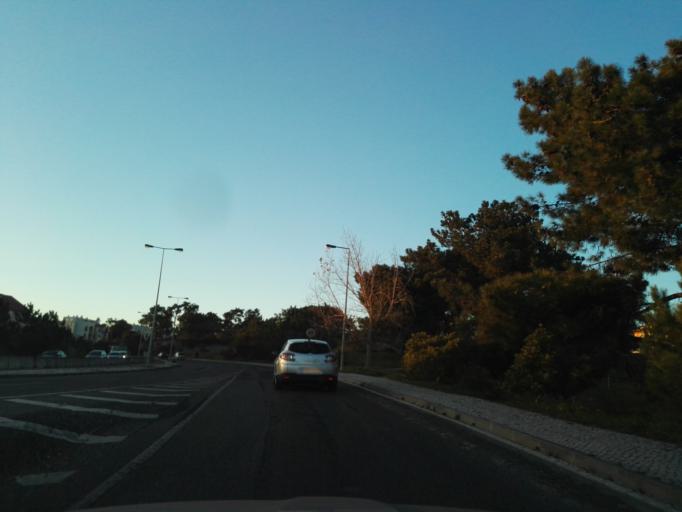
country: PT
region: Setubal
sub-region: Seixal
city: Corroios
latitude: 38.6439
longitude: -9.1496
